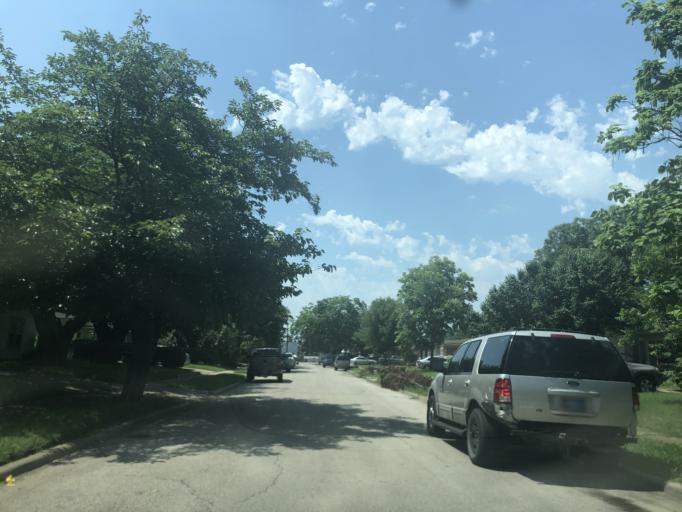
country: US
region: Texas
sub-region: Dallas County
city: Grand Prairie
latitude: 32.7301
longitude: -97.0131
